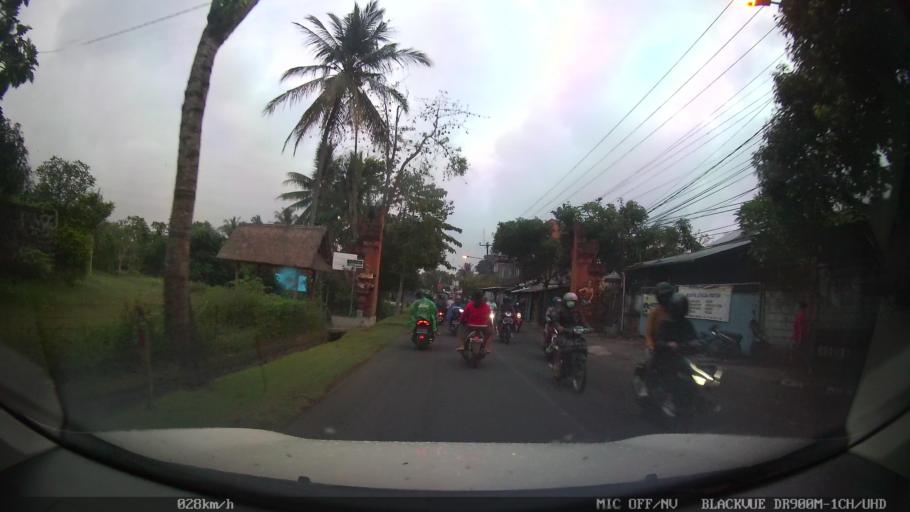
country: ID
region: Bali
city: Banjar Mambalkajanan
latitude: -8.5582
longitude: 115.2186
